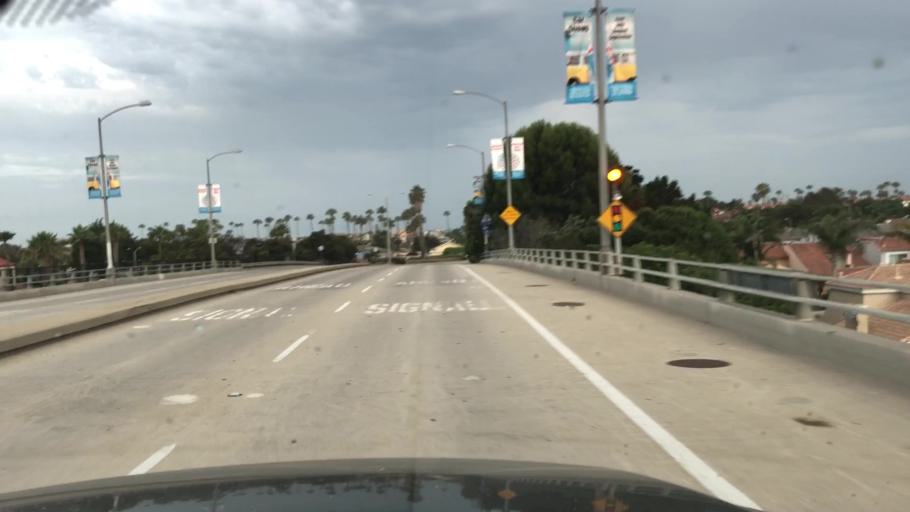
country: US
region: California
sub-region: Ventura County
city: Channel Islands Beach
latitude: 34.1758
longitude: -119.2281
